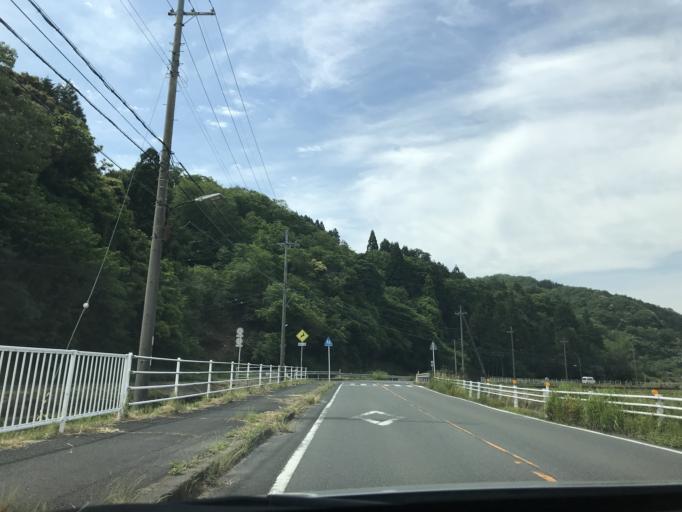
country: JP
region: Kyoto
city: Miyazu
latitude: 35.6634
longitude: 135.0236
